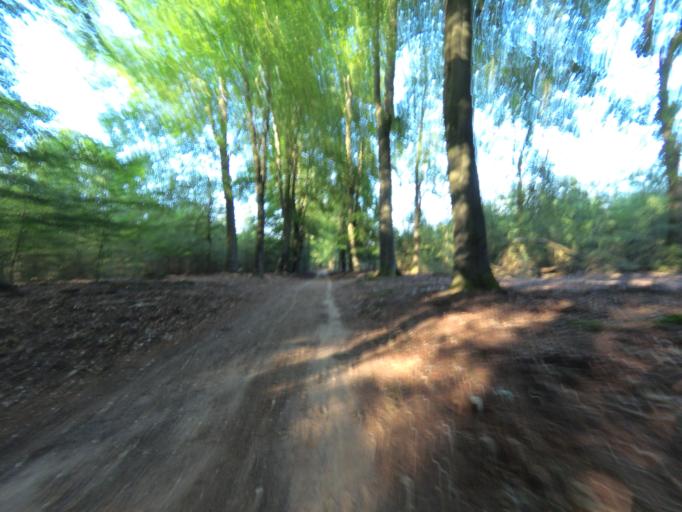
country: NL
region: Gelderland
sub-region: Gemeente Apeldoorn
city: Beekbergen
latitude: 52.1550
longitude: 5.9263
